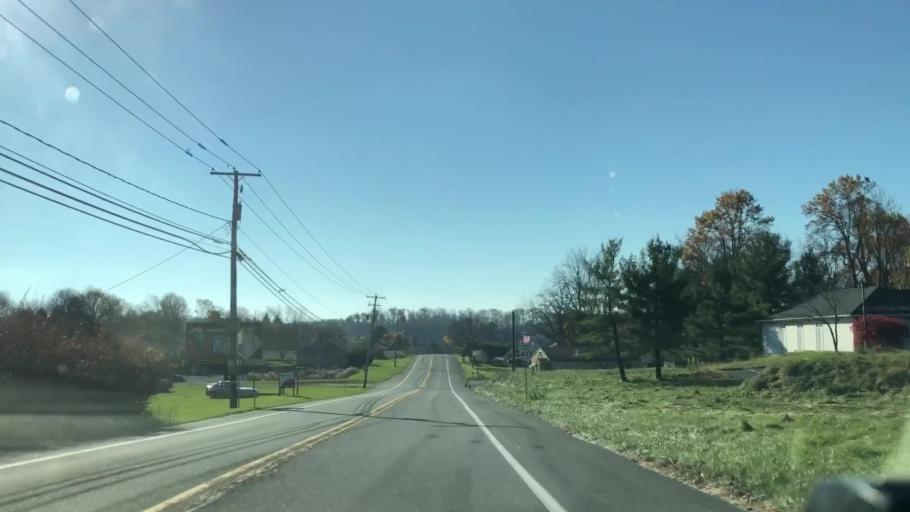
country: US
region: Pennsylvania
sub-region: Lehigh County
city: Macungie
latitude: 40.4883
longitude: -75.5236
